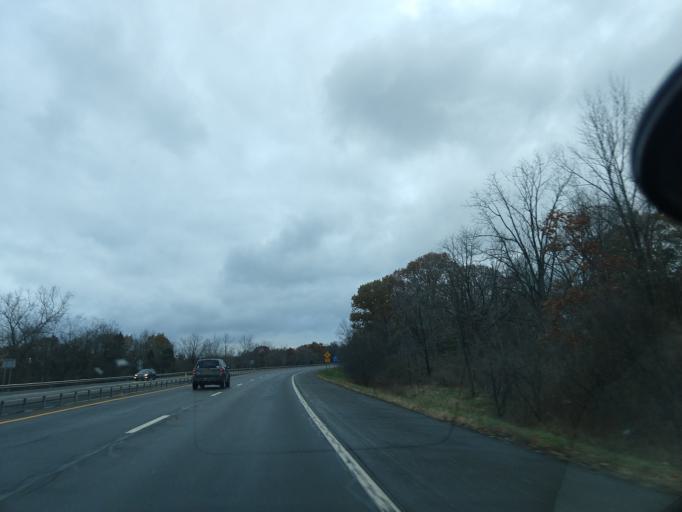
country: US
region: New York
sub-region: Tompkins County
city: Cayuga Heights
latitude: 42.4741
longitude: -76.5010
